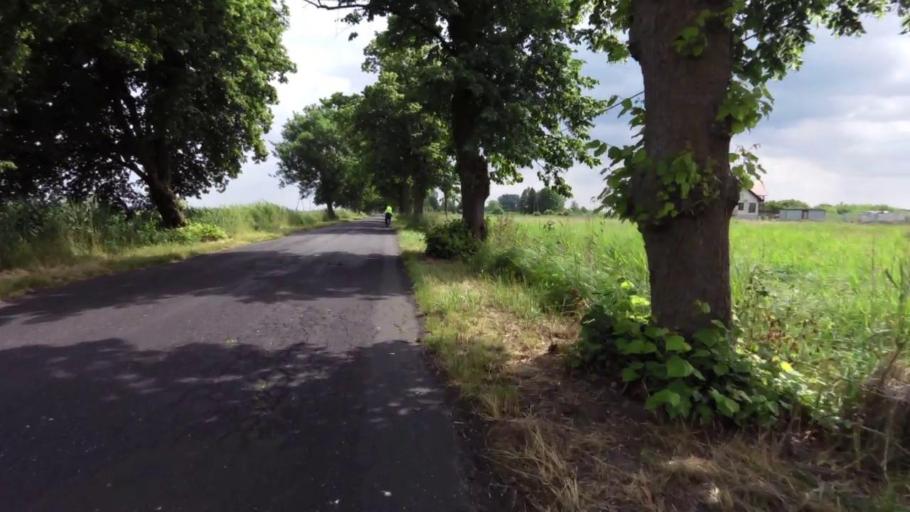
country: PL
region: West Pomeranian Voivodeship
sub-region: Powiat goleniowski
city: Stepnica
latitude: 53.6912
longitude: 14.5480
